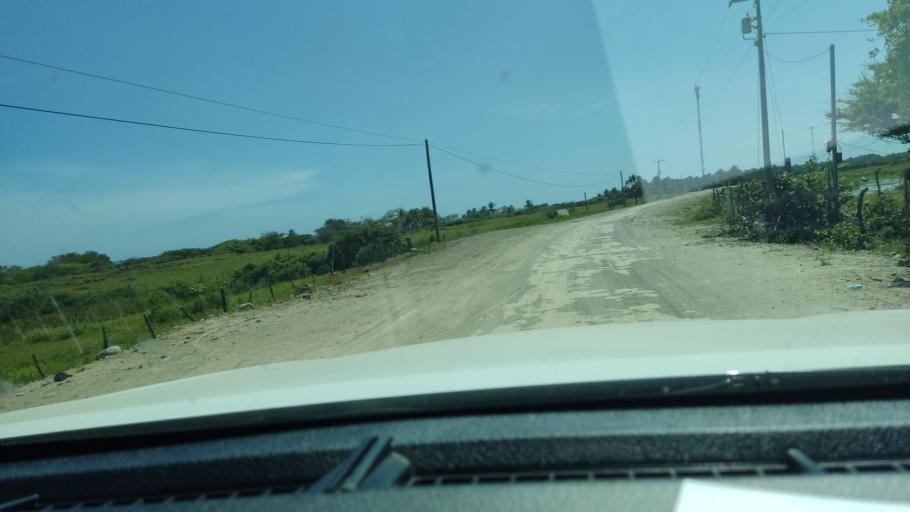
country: SV
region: Ahuachapan
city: San Francisco Menendez
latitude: 13.7660
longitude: -90.1735
